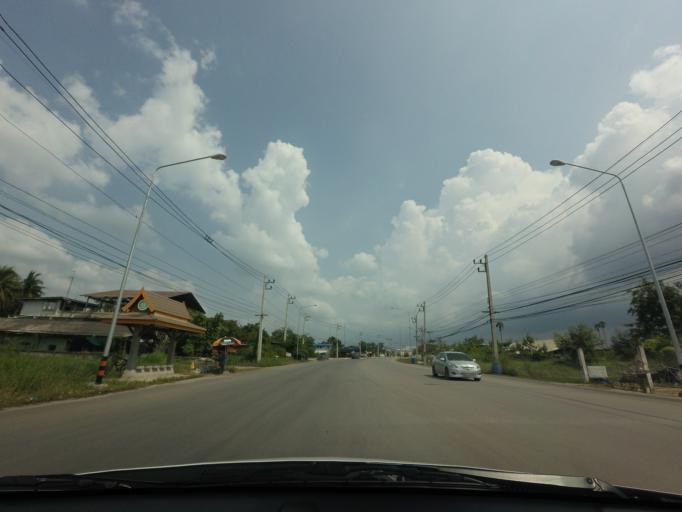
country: TH
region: Nakhon Pathom
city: Nakhon Chai Si
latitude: 13.8041
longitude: 100.2181
